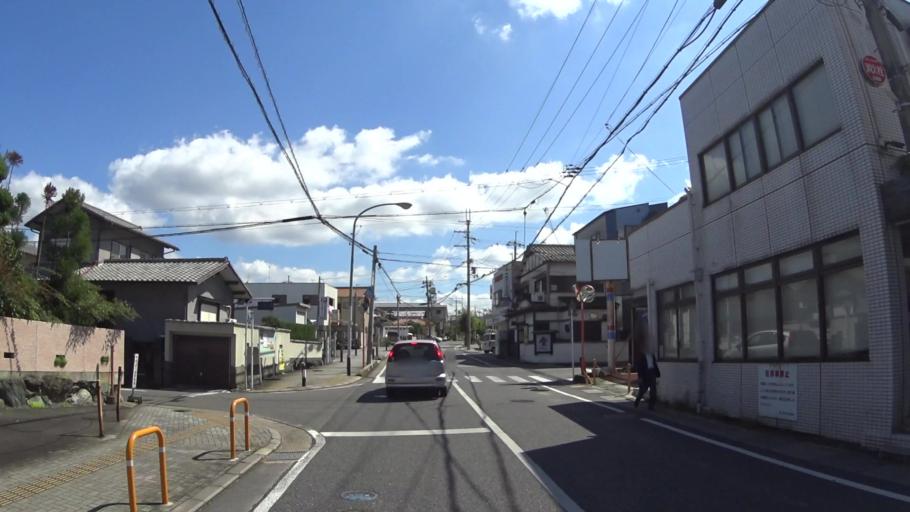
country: JP
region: Kyoto
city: Uji
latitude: 34.8850
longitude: 135.7850
